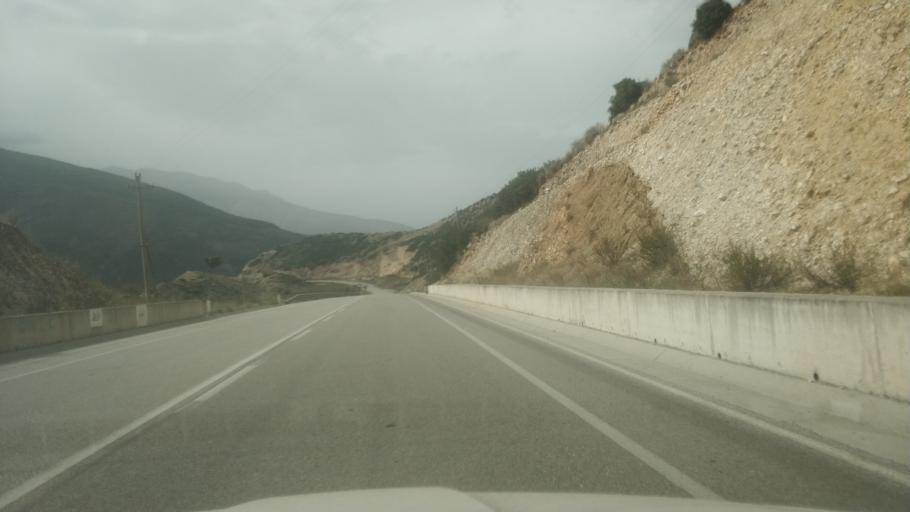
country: AL
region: Gjirokaster
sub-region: Rrethi i Tepelenes
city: Memaliaj
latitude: 40.3643
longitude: 19.9217
